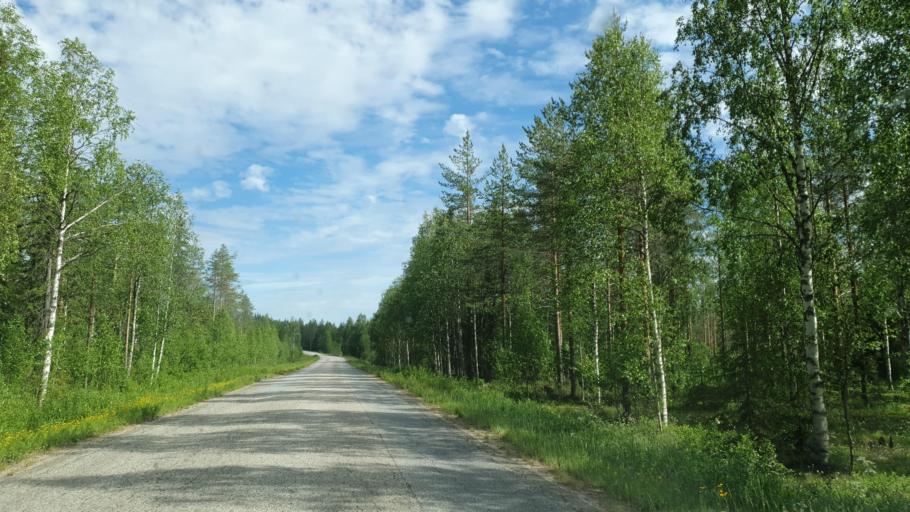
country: FI
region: Kainuu
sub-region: Kehys-Kainuu
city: Kuhmo
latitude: 64.5320
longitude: 29.3430
